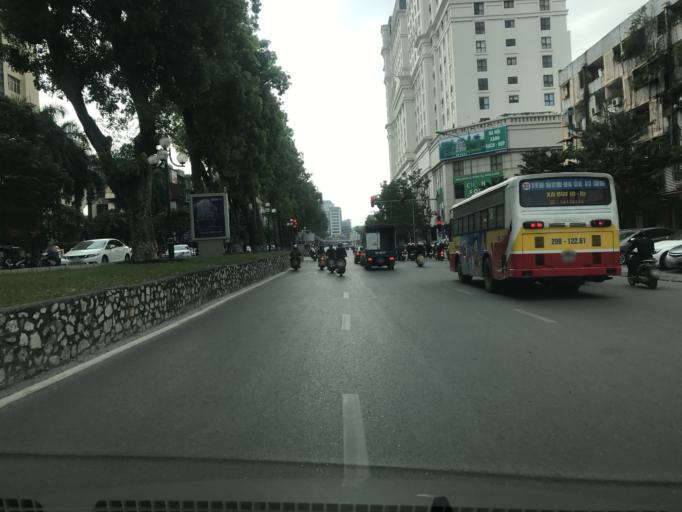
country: VN
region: Ha Noi
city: Dong Da
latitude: 21.0268
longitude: 105.8237
